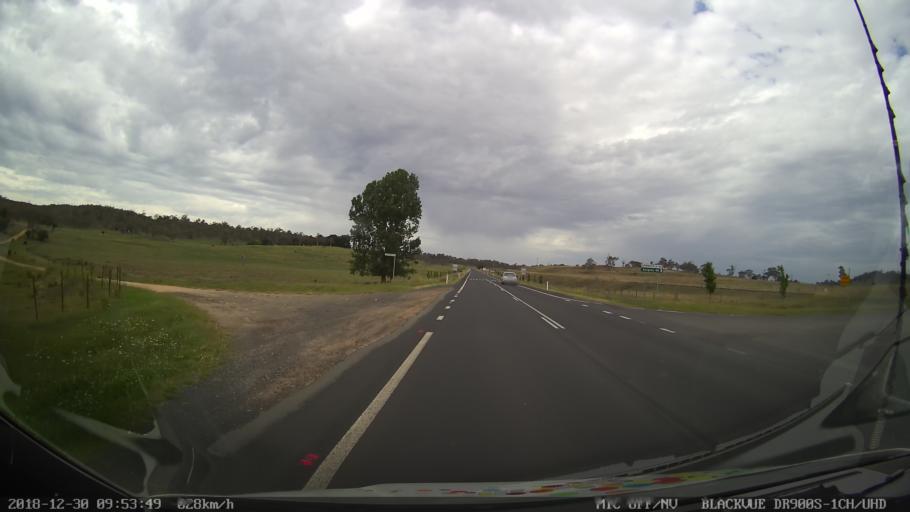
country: AU
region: New South Wales
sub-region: Cooma-Monaro
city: Cooma
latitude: -36.5181
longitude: 149.2810
